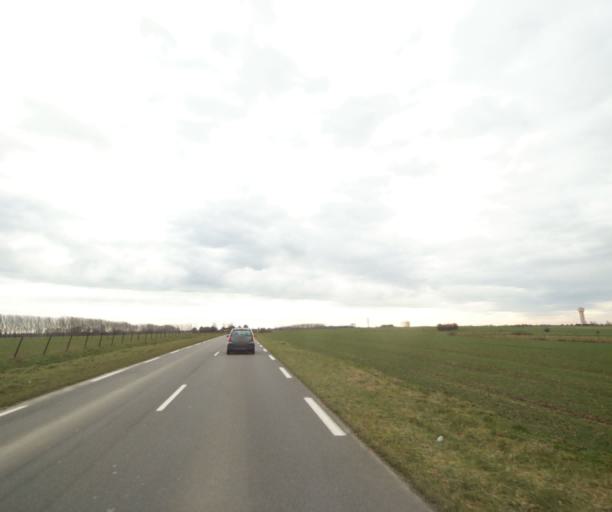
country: FR
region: Nord-Pas-de-Calais
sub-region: Departement du Nord
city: Curgies
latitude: 50.3234
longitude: 3.6143
